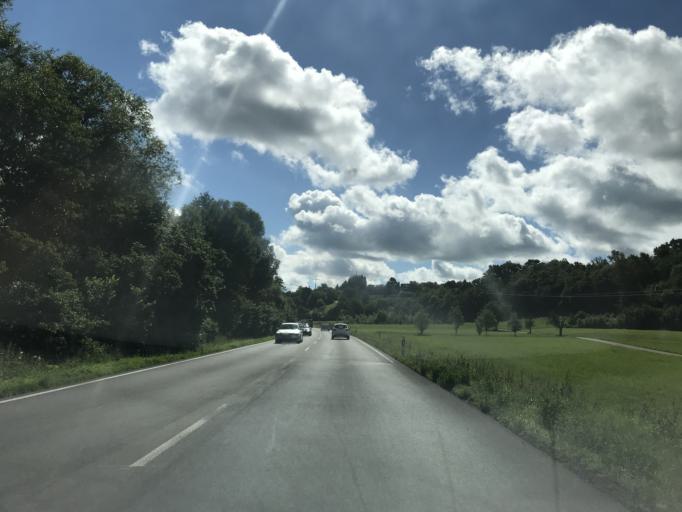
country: DE
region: Baden-Wuerttemberg
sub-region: Freiburg Region
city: Schopfheim
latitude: 47.6414
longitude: 7.8051
